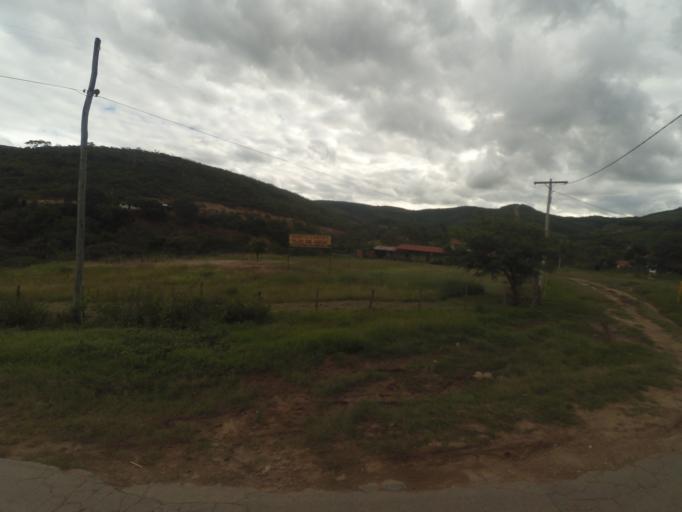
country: BO
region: Santa Cruz
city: Samaipata
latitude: -18.1706
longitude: -63.8304
